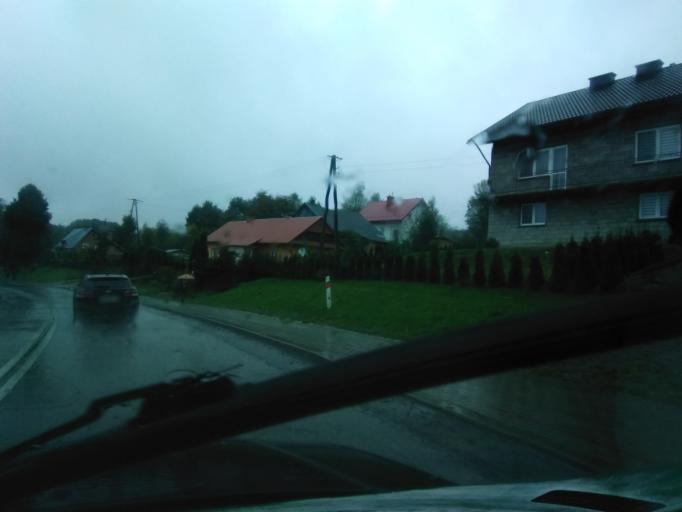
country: PL
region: Subcarpathian Voivodeship
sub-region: Powiat ropczycko-sedziszowski
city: Wielopole Skrzynskie
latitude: 49.9710
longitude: 21.5803
